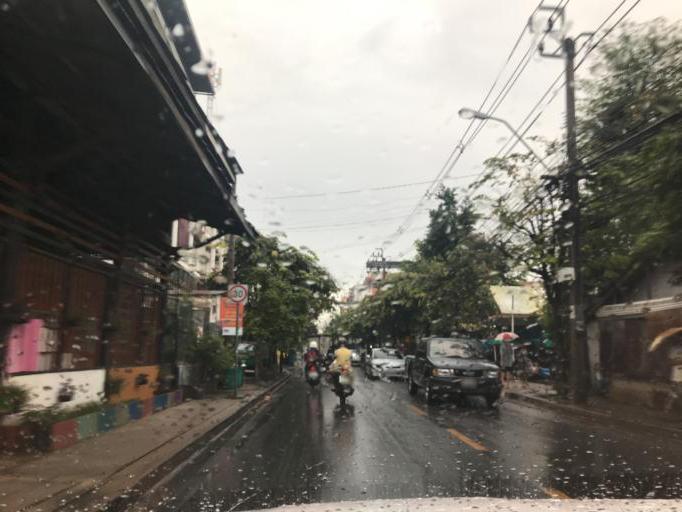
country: TH
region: Bangkok
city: Phasi Charoen
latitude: 13.7322
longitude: 100.4340
